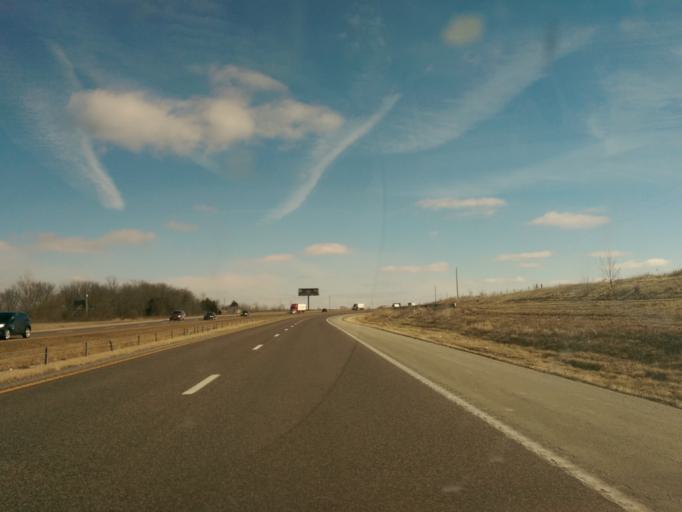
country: US
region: Missouri
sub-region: Callaway County
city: Fulton
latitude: 38.9435
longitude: -91.8830
